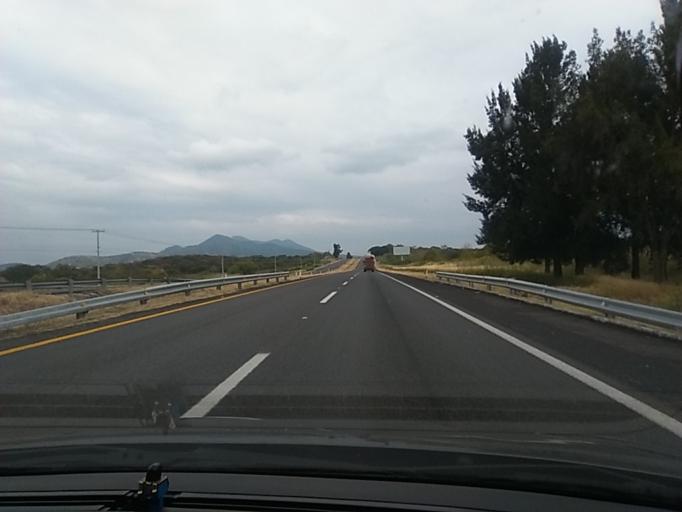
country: MX
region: Michoacan
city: Churintzio
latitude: 20.1531
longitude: -102.1023
